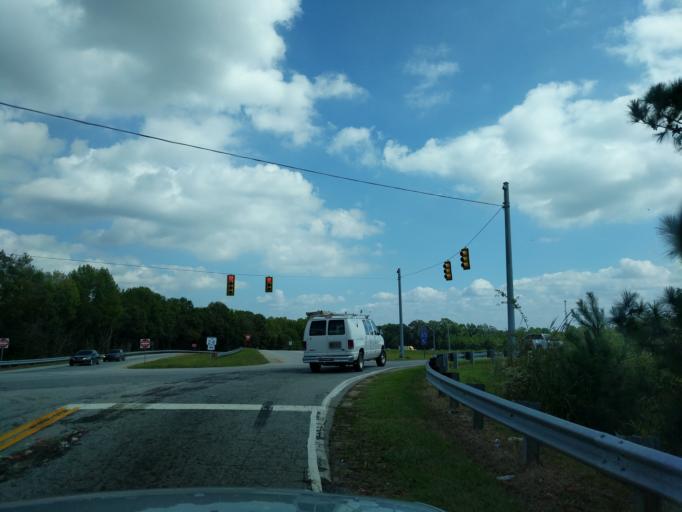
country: US
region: Georgia
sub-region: Hart County
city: Reed Creek
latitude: 34.5281
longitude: -82.8458
